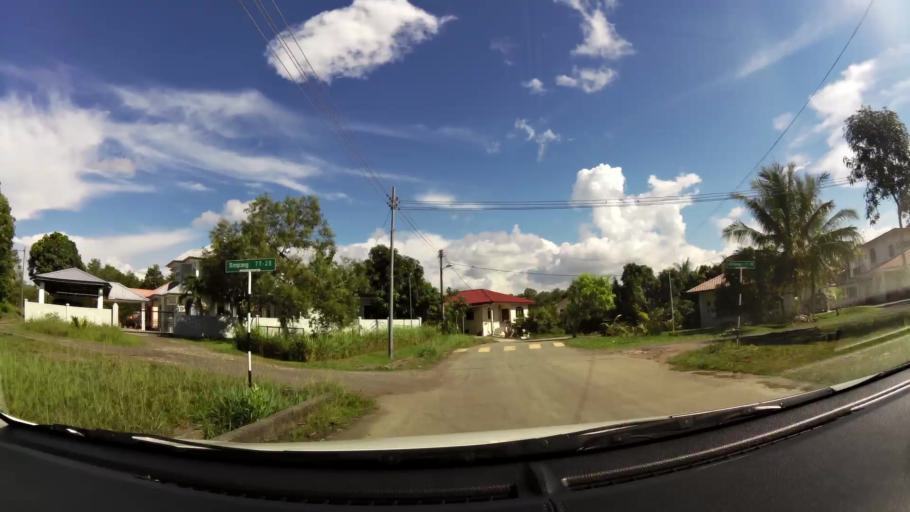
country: BN
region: Brunei and Muara
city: Bandar Seri Begawan
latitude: 4.9633
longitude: 114.9353
